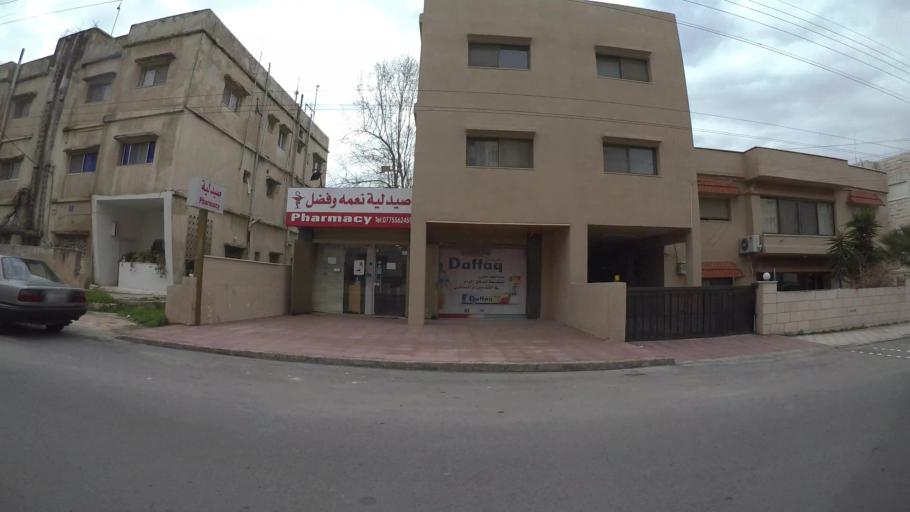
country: JO
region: Amman
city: Wadi as Sir
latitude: 31.9516
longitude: 35.8389
